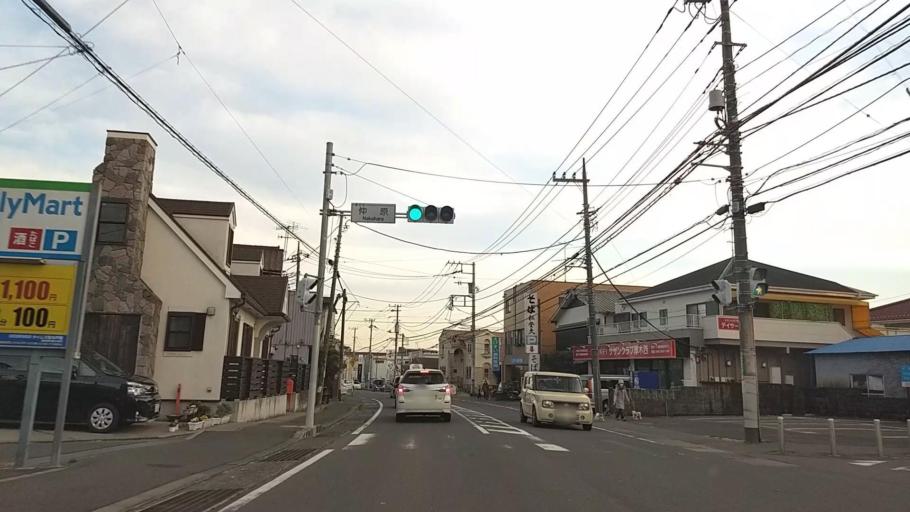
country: JP
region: Kanagawa
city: Atsugi
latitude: 35.4457
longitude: 139.3470
